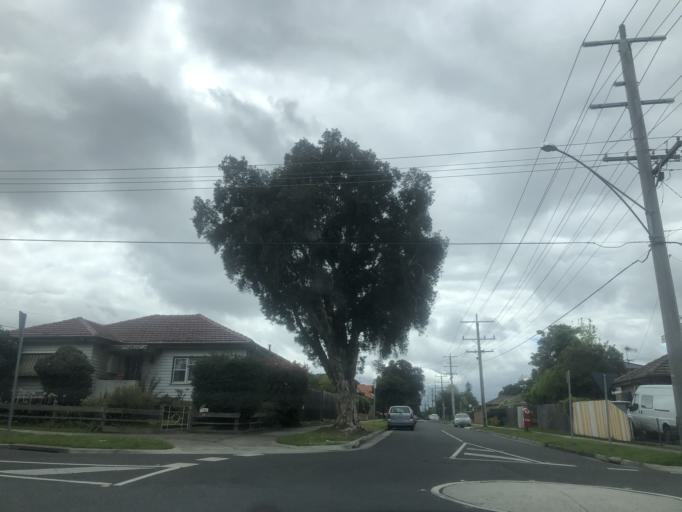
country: AU
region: Victoria
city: Clayton
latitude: -37.9171
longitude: 145.1159
